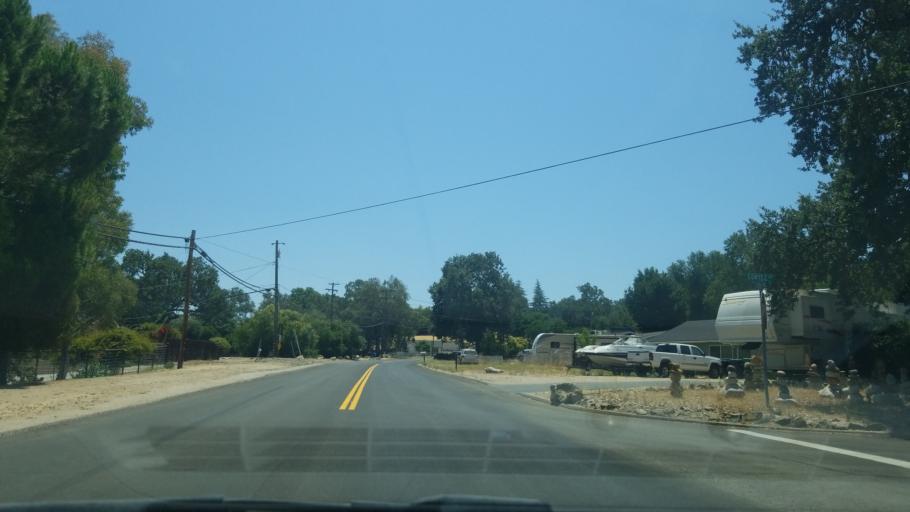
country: US
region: California
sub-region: San Luis Obispo County
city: Atascadero
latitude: 35.4878
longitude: -120.6480
